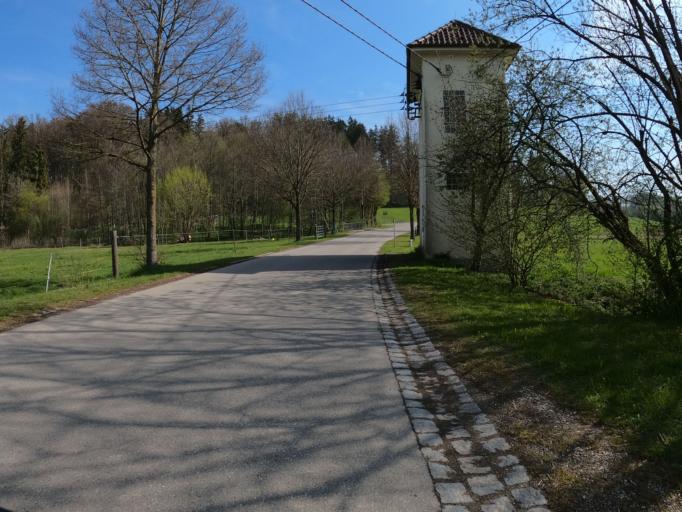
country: DE
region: Bavaria
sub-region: Swabia
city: Pfaffenhofen an der Roth
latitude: 48.3822
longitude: 10.1974
